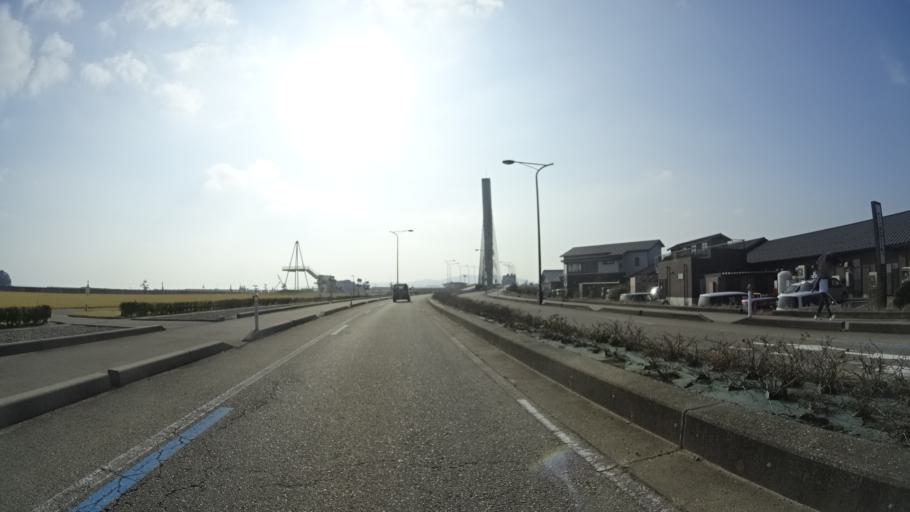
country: JP
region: Toyama
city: Himi
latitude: 36.8651
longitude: 136.9874
